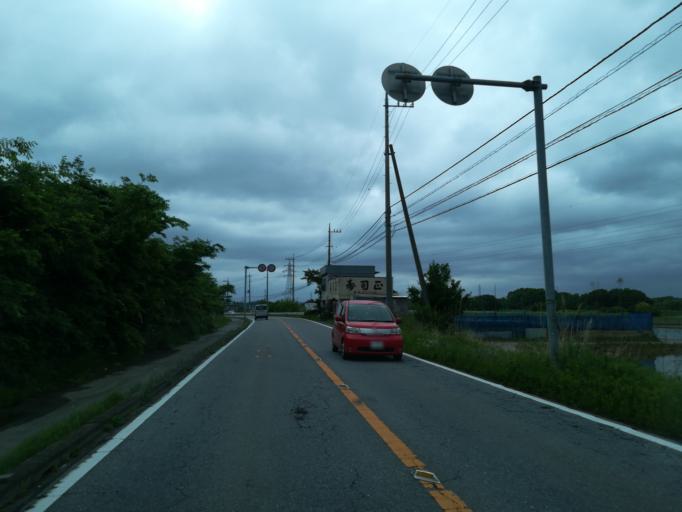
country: JP
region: Ibaraki
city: Tsukuba
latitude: 36.1838
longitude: 140.0790
